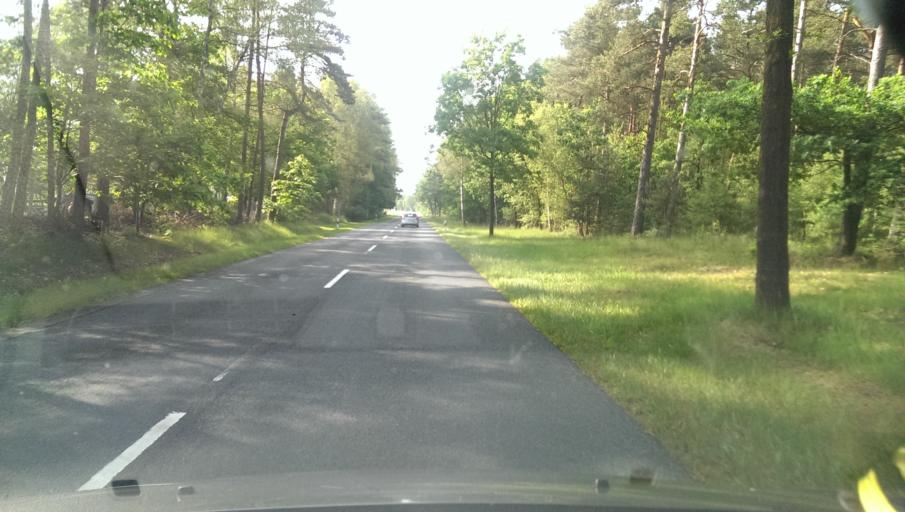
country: DE
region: Lower Saxony
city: Wietzendorf
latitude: 52.9301
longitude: 10.0017
